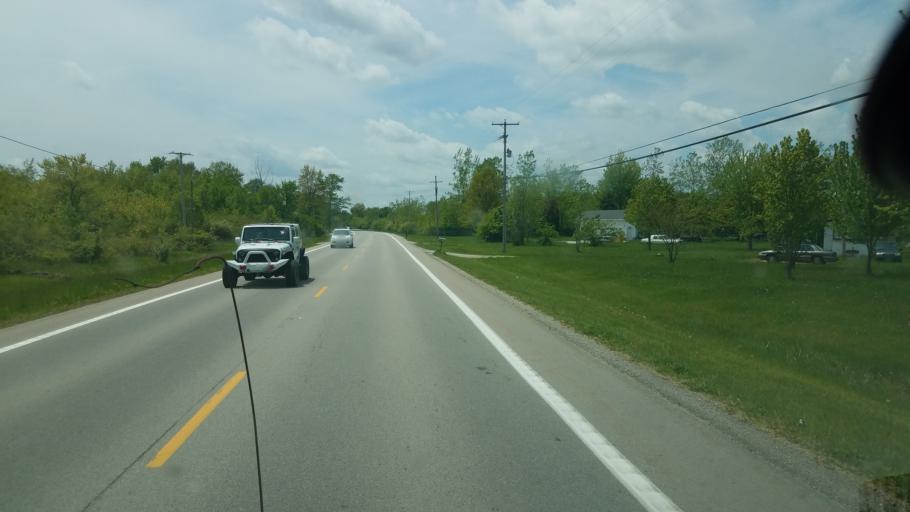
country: US
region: Ohio
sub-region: Ottawa County
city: Port Clinton
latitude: 41.4695
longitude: -83.0382
